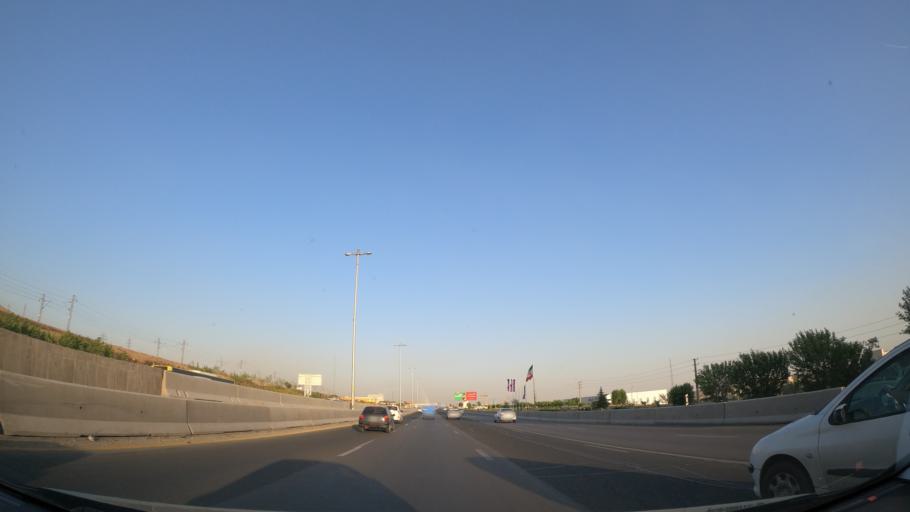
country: IR
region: Tehran
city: Shahr-e Qods
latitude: 35.7552
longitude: 51.0729
